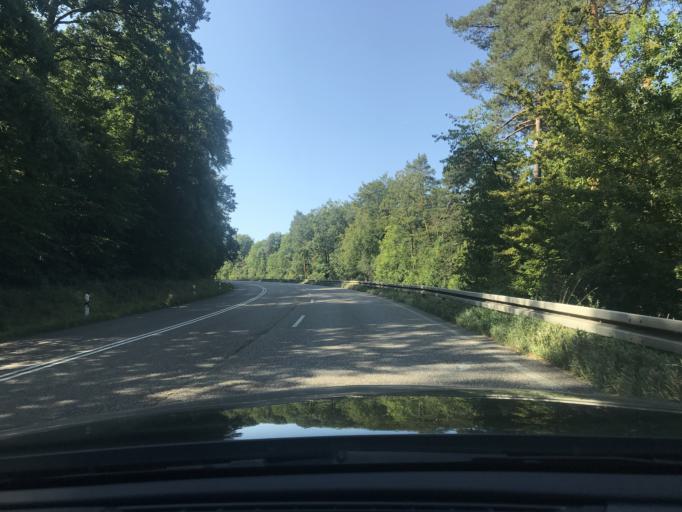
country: DE
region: Baden-Wuerttemberg
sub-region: Regierungsbezirk Stuttgart
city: Ostfildern
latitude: 48.7539
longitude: 9.2343
